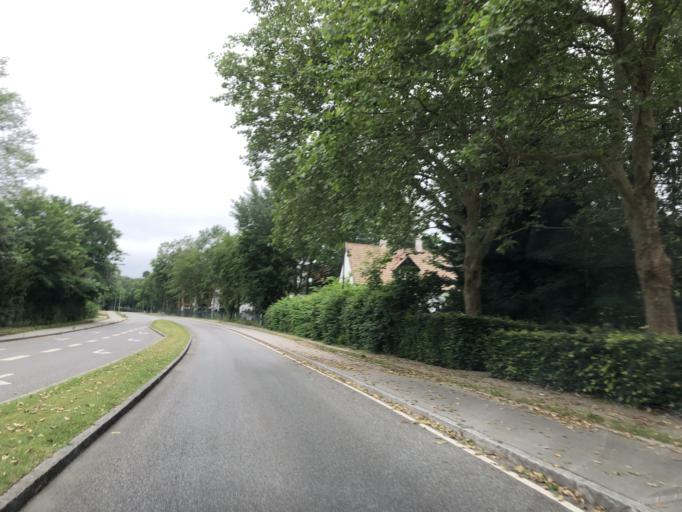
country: DK
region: Capital Region
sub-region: Lyngby-Tarbaek Kommune
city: Kongens Lyngby
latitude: 55.8095
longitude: 12.5101
